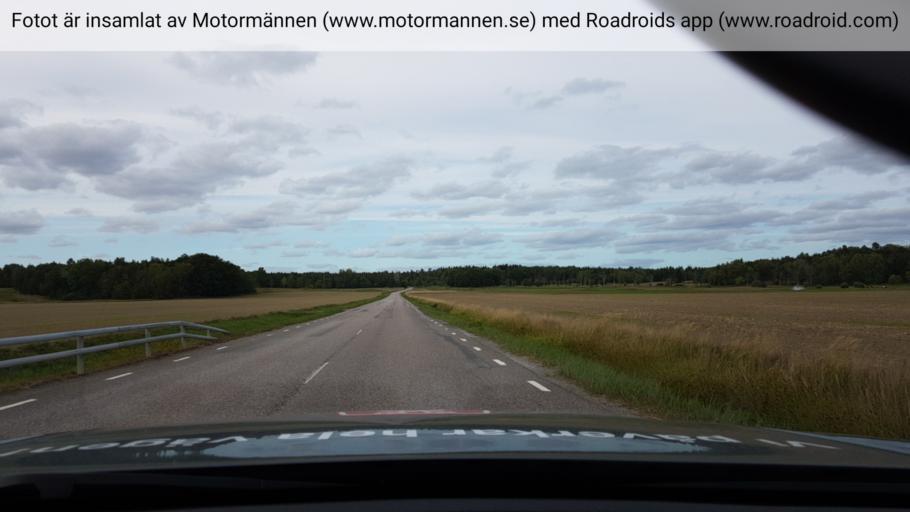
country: SE
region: Stockholm
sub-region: Haninge Kommun
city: Haninge
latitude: 59.1053
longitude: 18.1870
